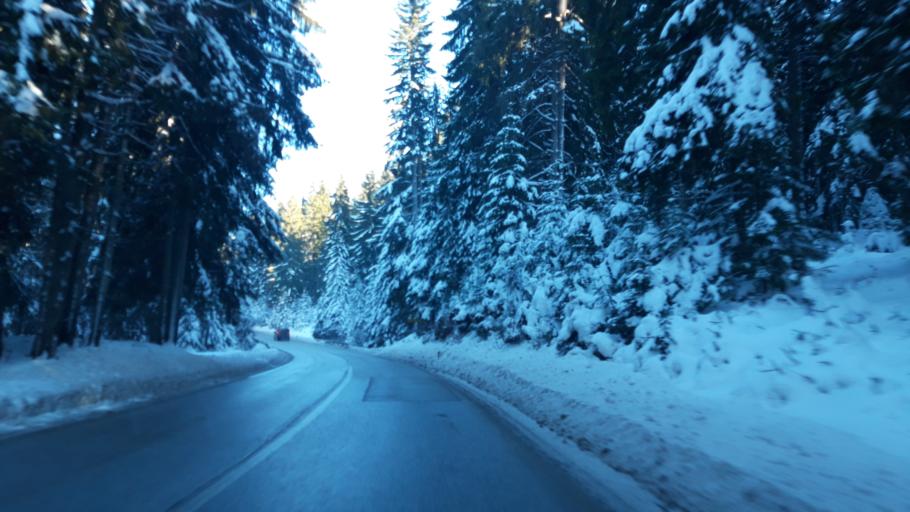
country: BA
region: Republika Srpska
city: Pale
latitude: 43.9254
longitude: 18.6592
